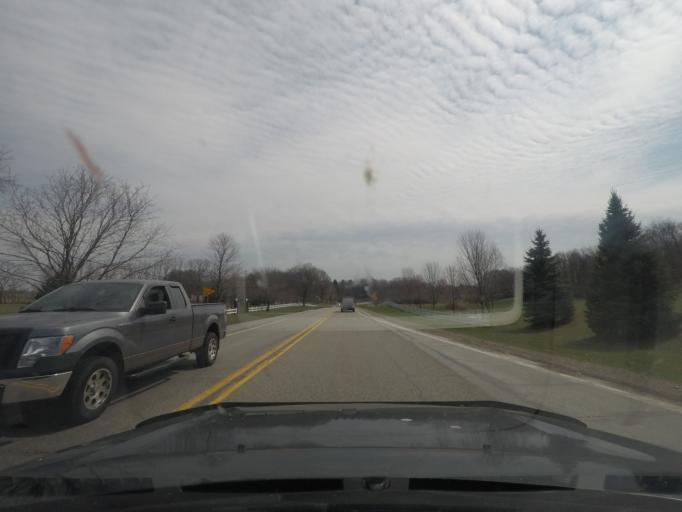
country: US
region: Indiana
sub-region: LaPorte County
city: LaPorte
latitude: 41.6456
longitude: -86.7508
